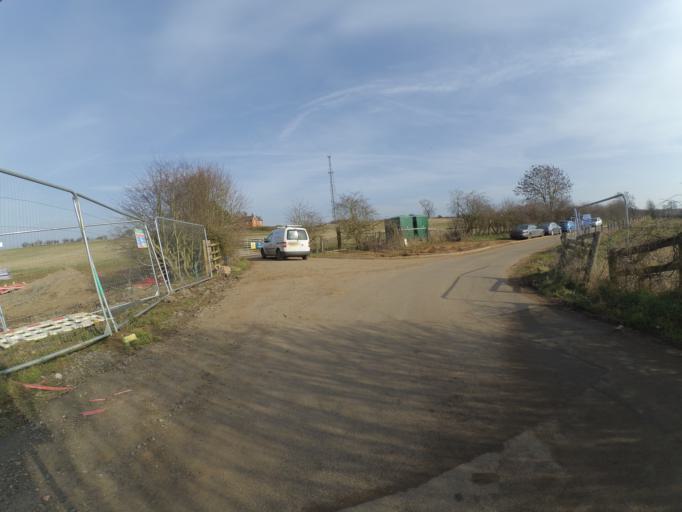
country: GB
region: England
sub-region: Warwickshire
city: Rugby
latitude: 52.3616
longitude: -1.2046
